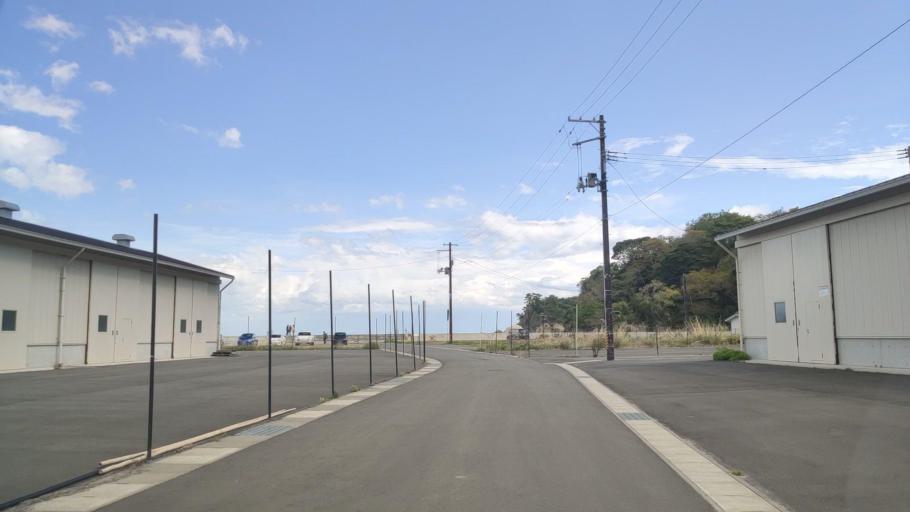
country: JP
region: Miyagi
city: Matsushima
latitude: 38.3251
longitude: 141.1543
